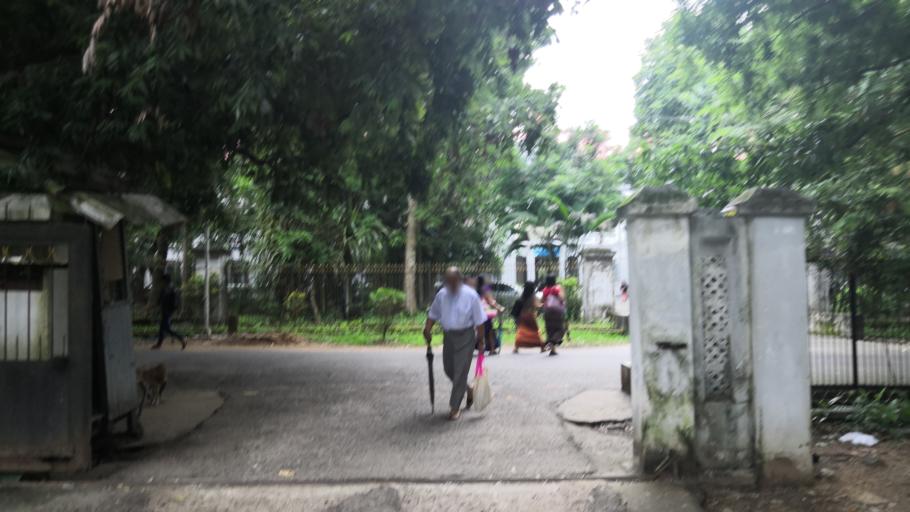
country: MM
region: Yangon
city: Yangon
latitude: 16.8286
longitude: 96.1331
